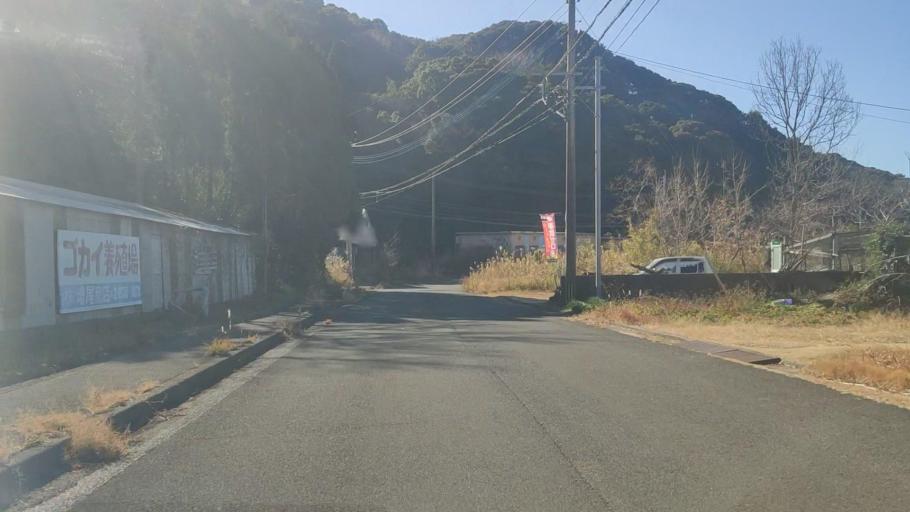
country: JP
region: Oita
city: Saiki
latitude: 32.7981
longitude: 131.8999
